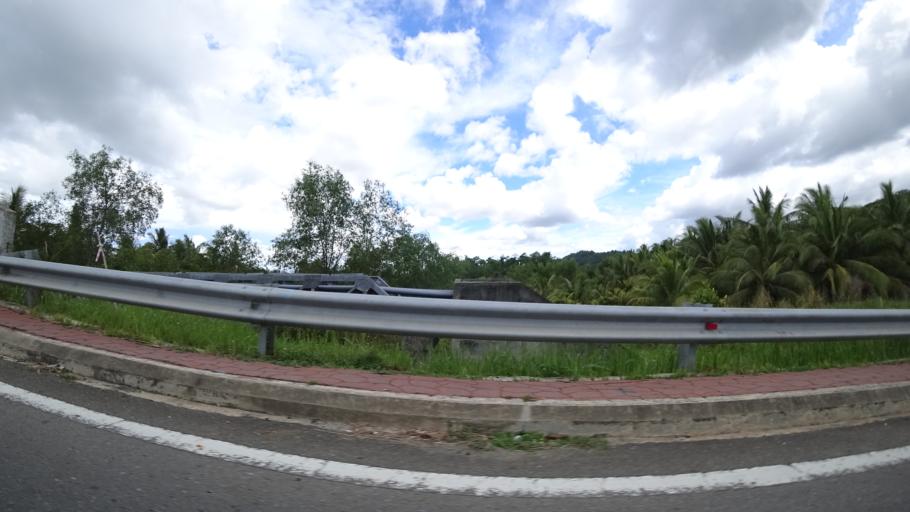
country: BN
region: Brunei and Muara
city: Bandar Seri Begawan
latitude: 4.9700
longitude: 115.0229
